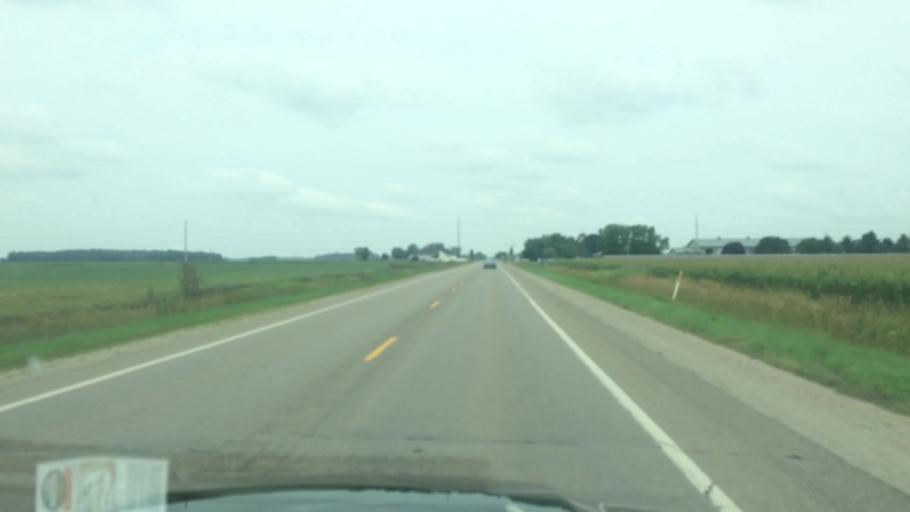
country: US
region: Michigan
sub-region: Huron County
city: Bad Axe
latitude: 43.8335
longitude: -83.0013
